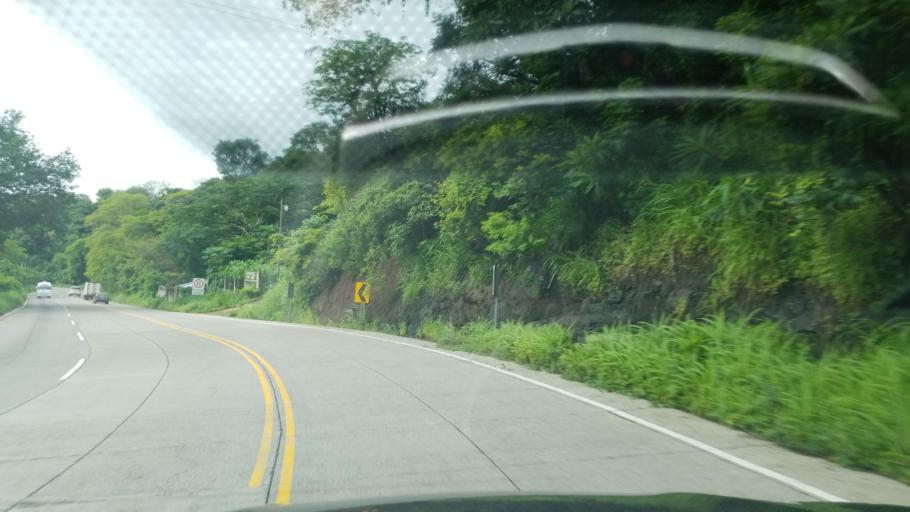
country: HN
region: Francisco Morazan
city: El Porvenir
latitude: 13.7085
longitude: -87.3188
